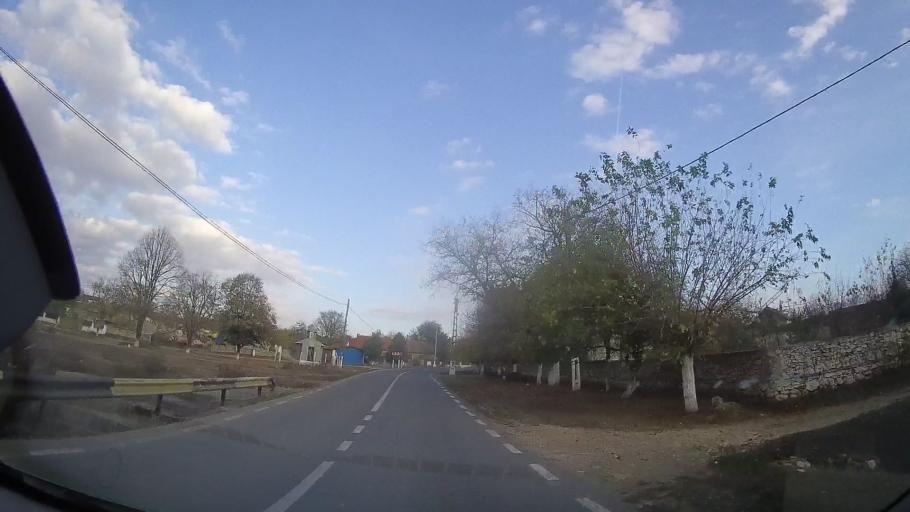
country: RO
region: Constanta
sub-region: Comuna Chirnogeni
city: Plopeni
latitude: 43.9618
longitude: 28.1410
